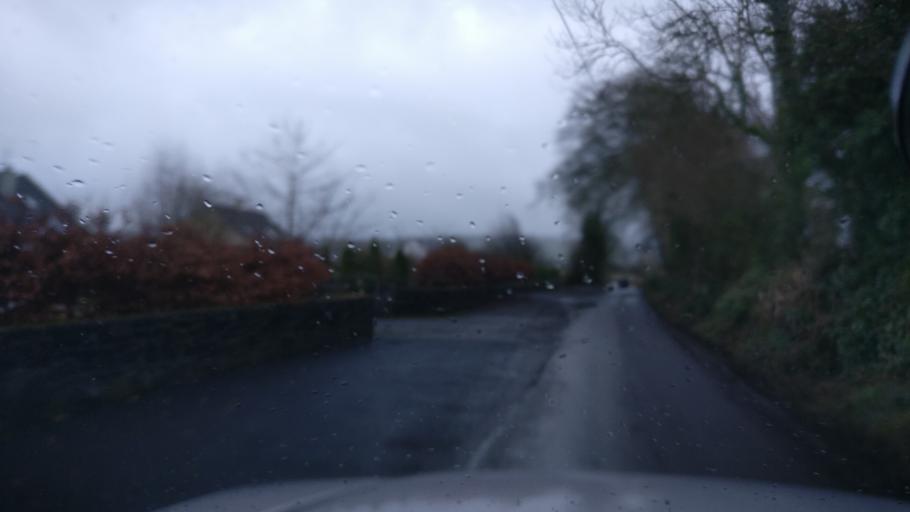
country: IE
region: Connaught
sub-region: County Galway
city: Loughrea
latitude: 53.1958
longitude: -8.6632
